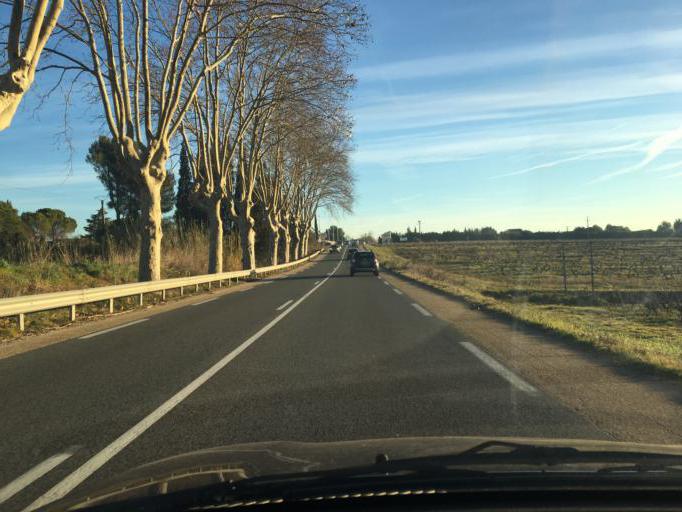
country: FR
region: Provence-Alpes-Cote d'Azur
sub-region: Departement du Var
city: La Motte
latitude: 43.4628
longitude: 6.5311
